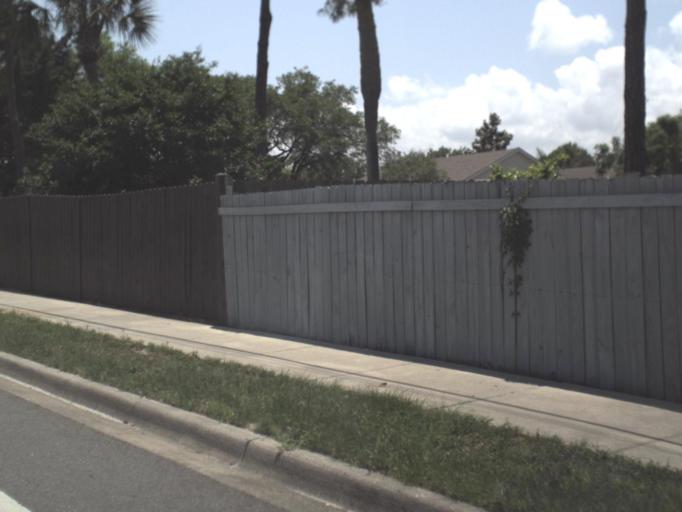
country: US
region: Florida
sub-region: Saint Johns County
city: Saint Augustine Beach
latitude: 29.8640
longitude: -81.2821
